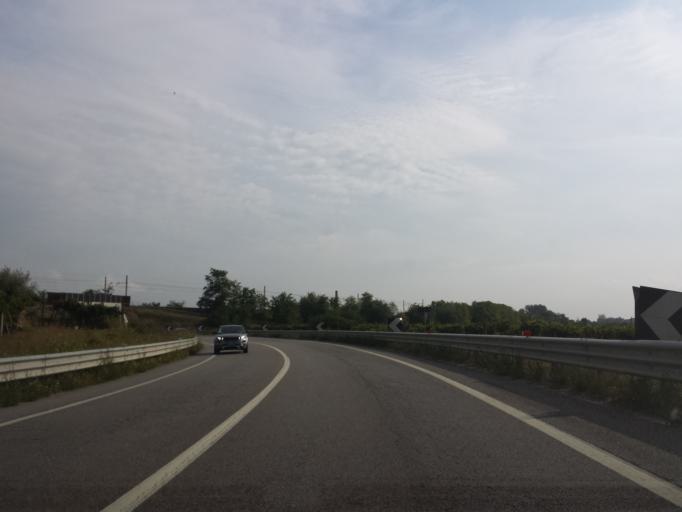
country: IT
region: Veneto
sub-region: Provincia di Verona
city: Soave
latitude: 45.4010
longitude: 11.2517
